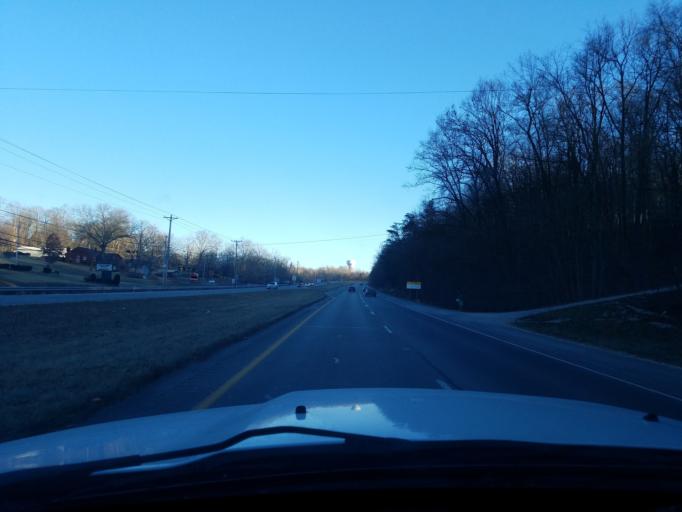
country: US
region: Indiana
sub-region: Floyd County
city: Galena
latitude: 38.3405
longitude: -85.9092
